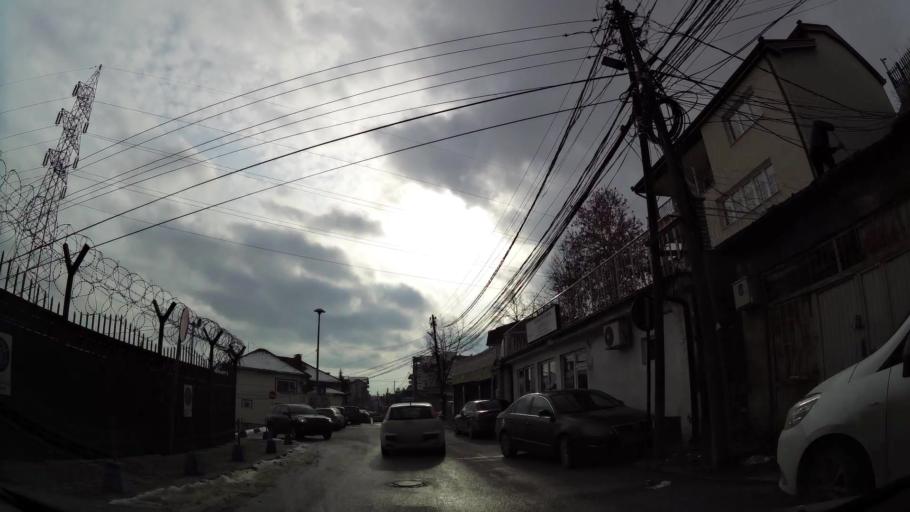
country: XK
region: Pristina
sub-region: Komuna e Prishtines
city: Pristina
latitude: 42.6653
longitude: 21.1522
